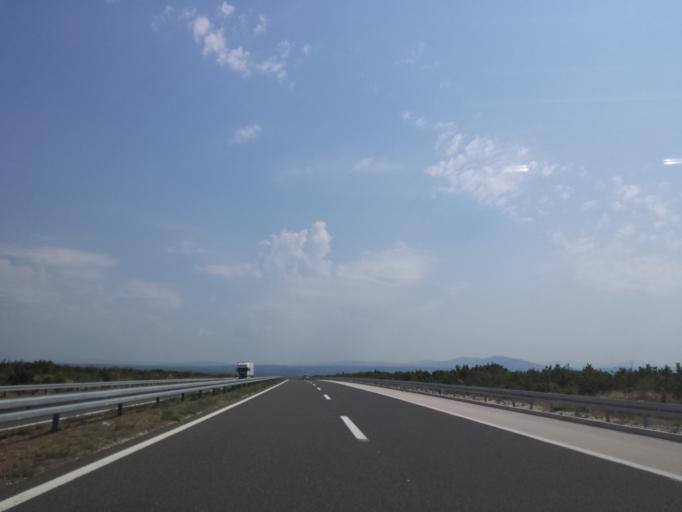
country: HR
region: Sibensko-Kniniska
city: Zaton
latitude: 43.8621
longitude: 15.8236
